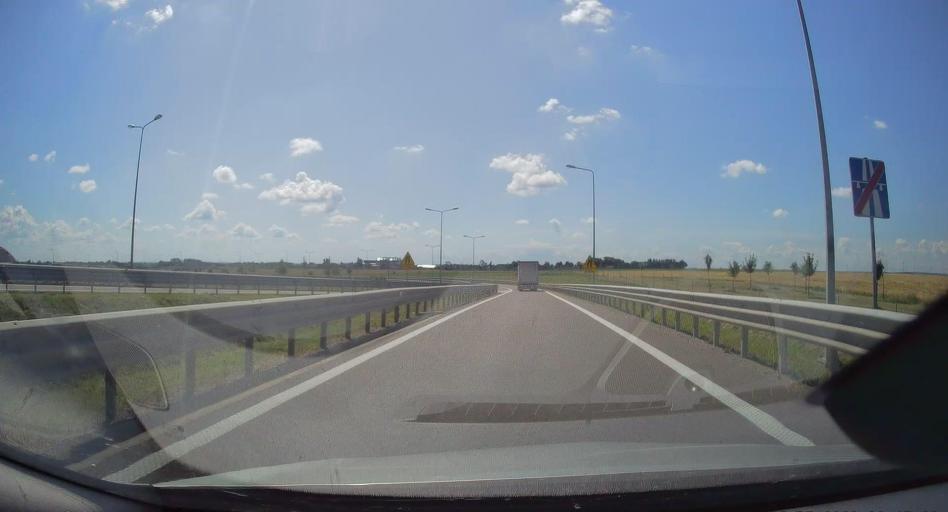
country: PL
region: Subcarpathian Voivodeship
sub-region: Powiat jaroslawski
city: Radymno
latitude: 49.9102
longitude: 22.8097
